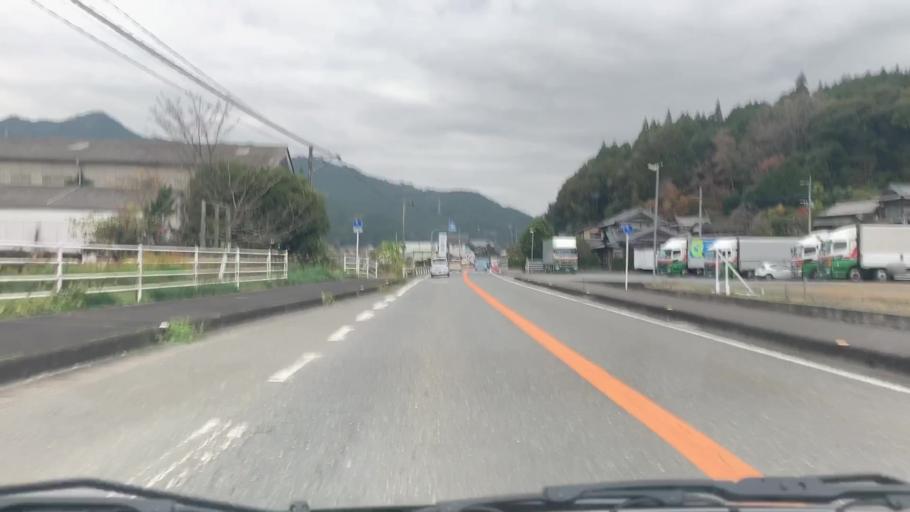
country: JP
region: Saga Prefecture
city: Ureshinomachi-shimojuku
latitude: 33.1269
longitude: 130.0396
